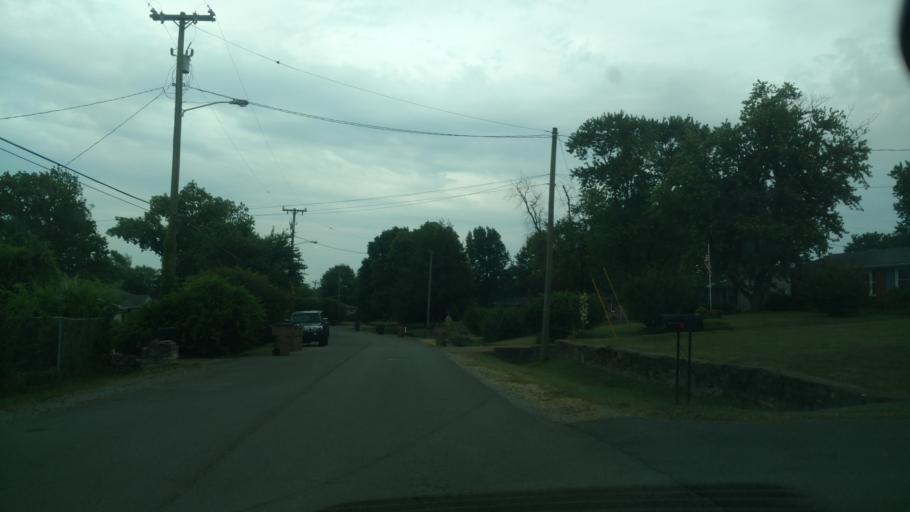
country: US
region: Tennessee
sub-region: Davidson County
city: Nashville
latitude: 36.1990
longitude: -86.7077
